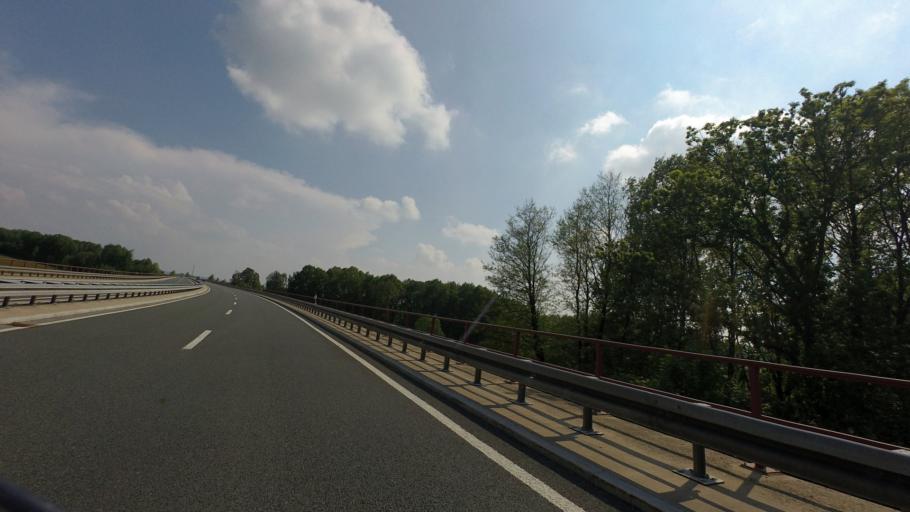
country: DE
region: Saxony
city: Lobau
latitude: 51.1246
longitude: 14.6469
